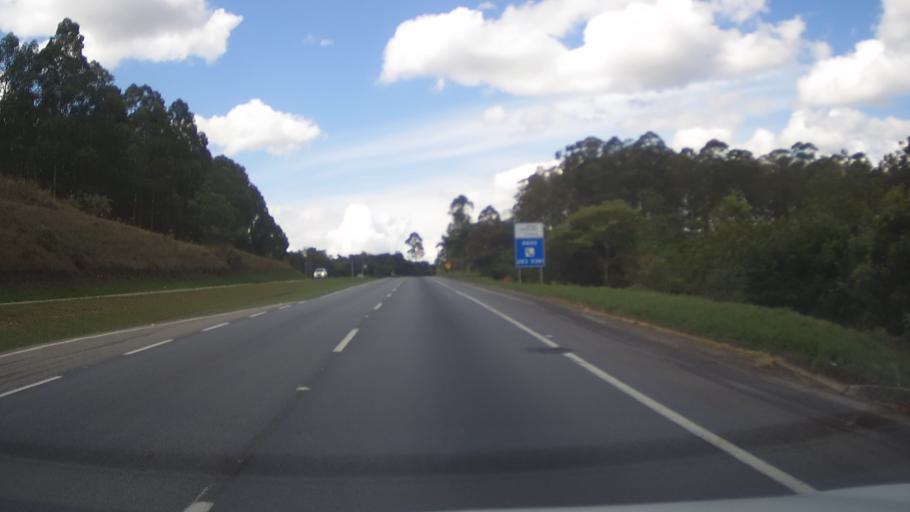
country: BR
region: Minas Gerais
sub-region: Santo Antonio Do Amparo
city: Santo Antonio do Amparo
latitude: -20.8503
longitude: -44.8345
